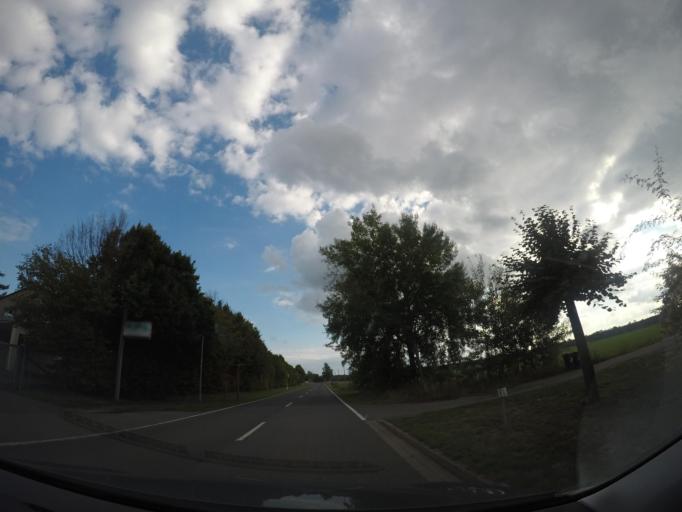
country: DE
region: Saxony-Anhalt
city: Mieste
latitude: 52.4569
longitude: 11.1419
